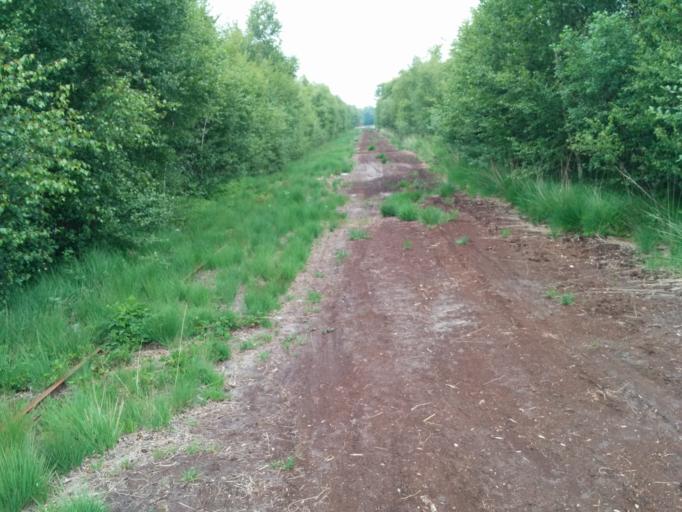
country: DE
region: Lower Saxony
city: Lohne
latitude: 52.6513
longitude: 8.2806
